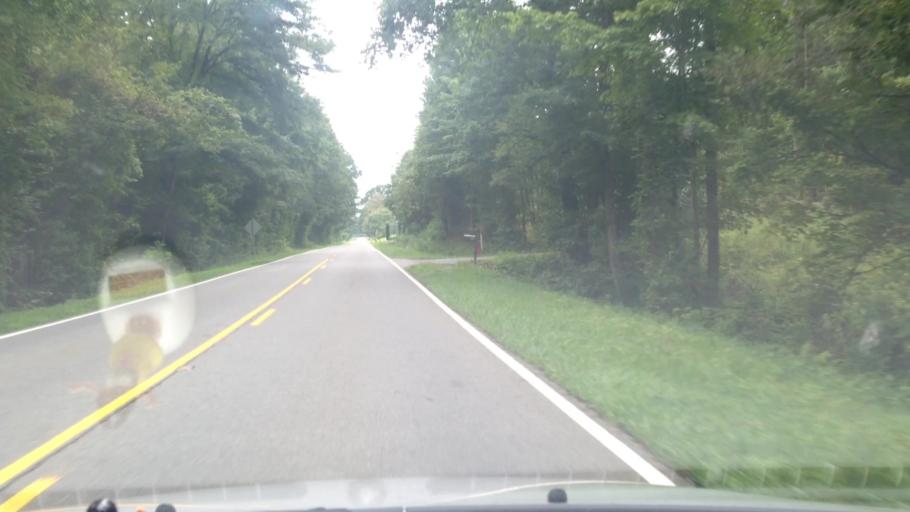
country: US
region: North Carolina
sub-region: Stokes County
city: Walnut Cove
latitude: 36.2724
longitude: -80.1447
